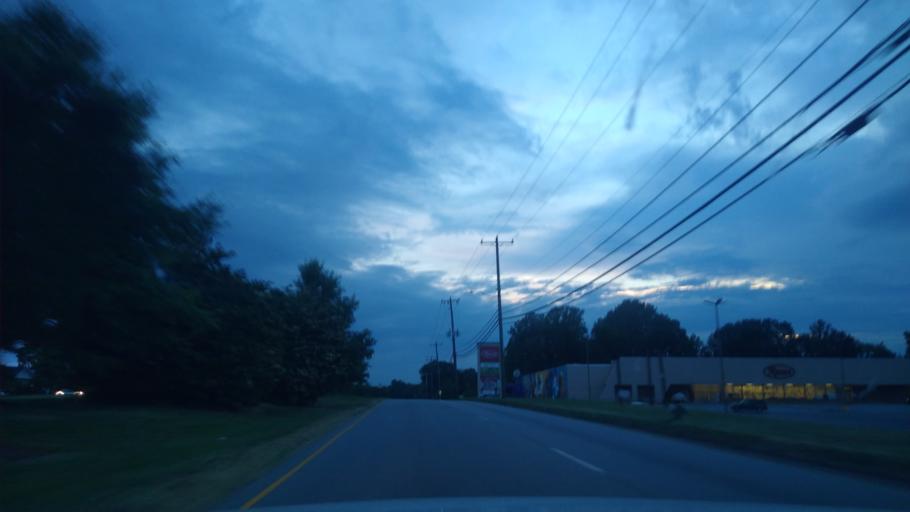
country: US
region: North Carolina
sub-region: Guilford County
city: Greensboro
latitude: 36.1134
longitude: -79.7661
